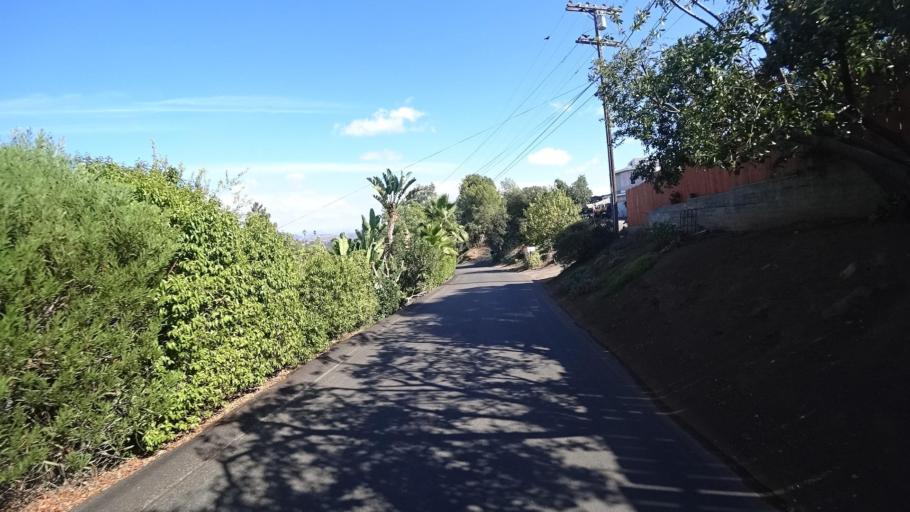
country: US
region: California
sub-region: San Diego County
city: Casa de Oro-Mount Helix
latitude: 32.7629
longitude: -116.9637
